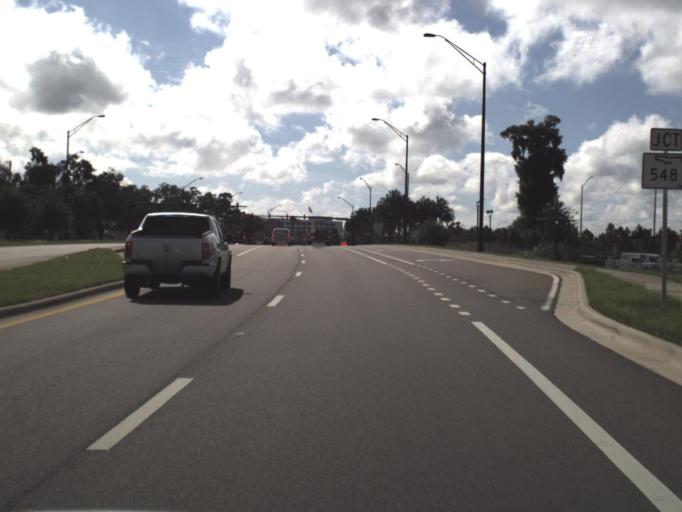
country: US
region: Florida
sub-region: Polk County
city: Lakeland
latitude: 28.0493
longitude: -81.9652
